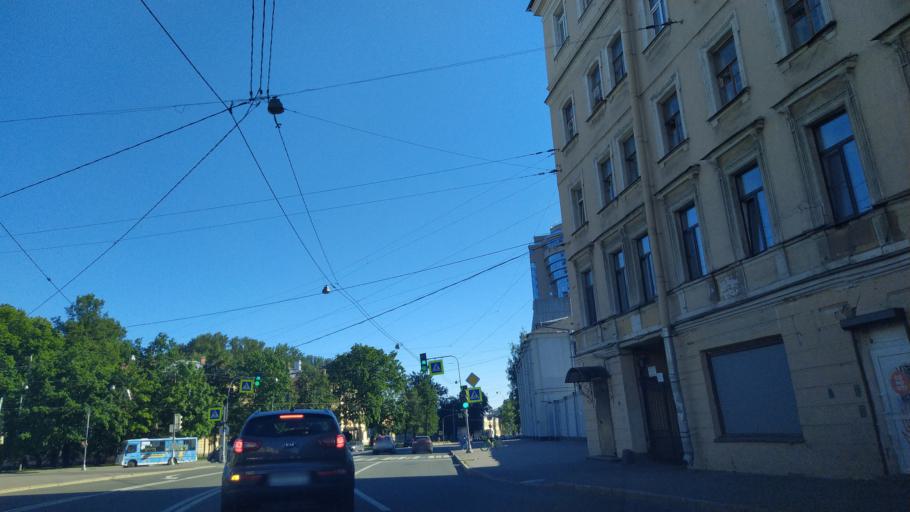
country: RU
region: Leningrad
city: Finlyandskiy
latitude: 59.9598
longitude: 30.3454
